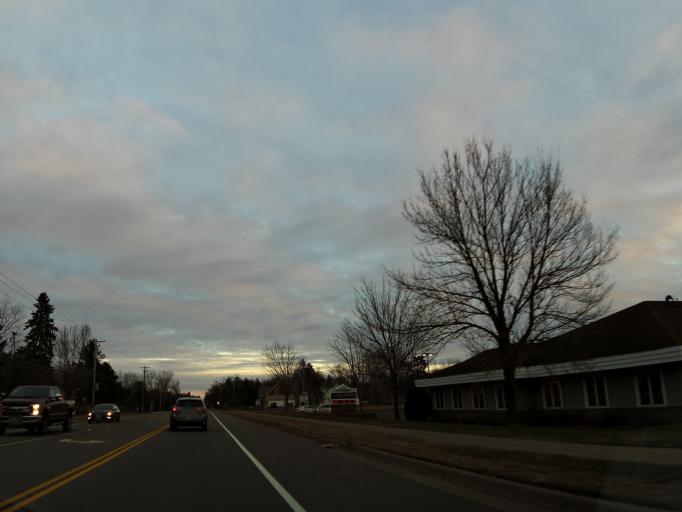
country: US
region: Minnesota
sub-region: Ramsey County
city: White Bear Lake
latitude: 45.0503
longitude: -93.0276
